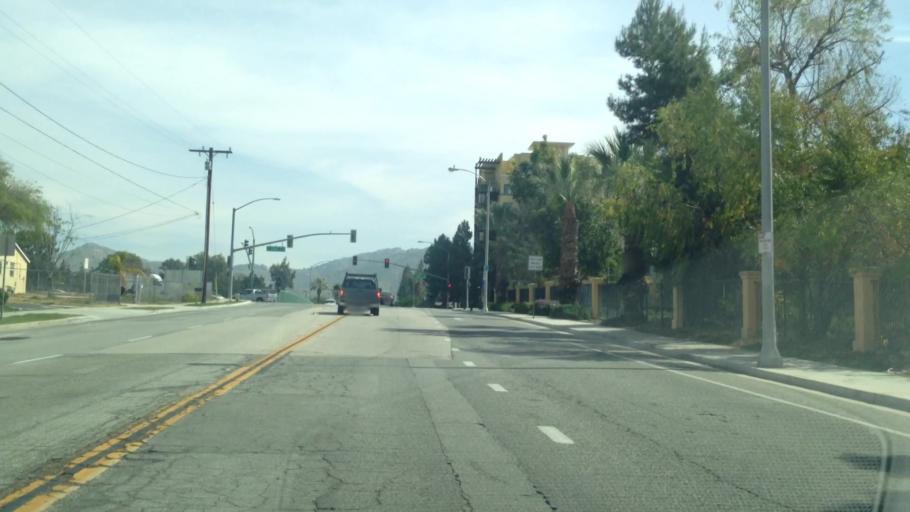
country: US
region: California
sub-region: Riverside County
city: Highgrove
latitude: 33.9793
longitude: -117.3412
